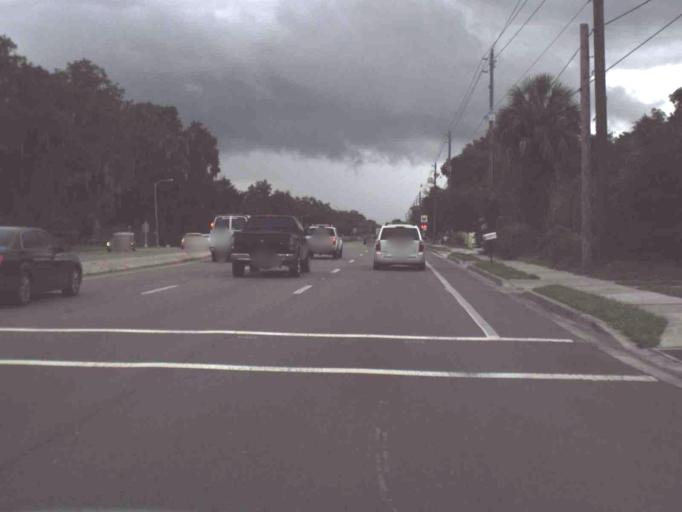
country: US
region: Florida
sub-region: Manatee County
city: Samoset
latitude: 27.4960
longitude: -82.5446
